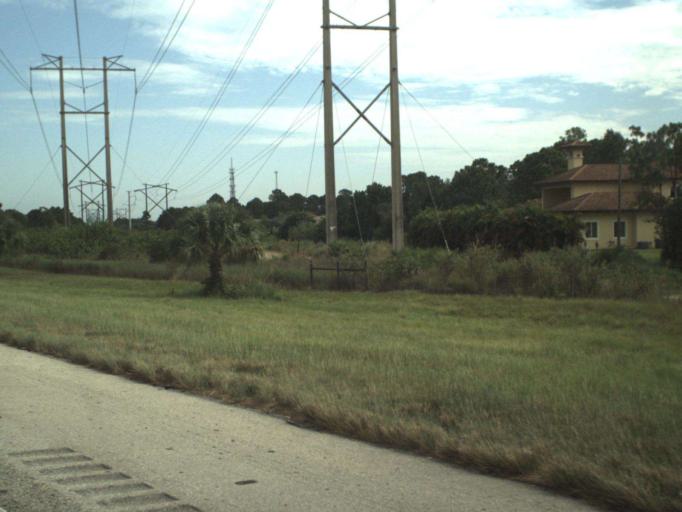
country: US
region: Florida
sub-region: Saint Lucie County
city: Port Saint Lucie
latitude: 27.2493
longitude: -80.4156
